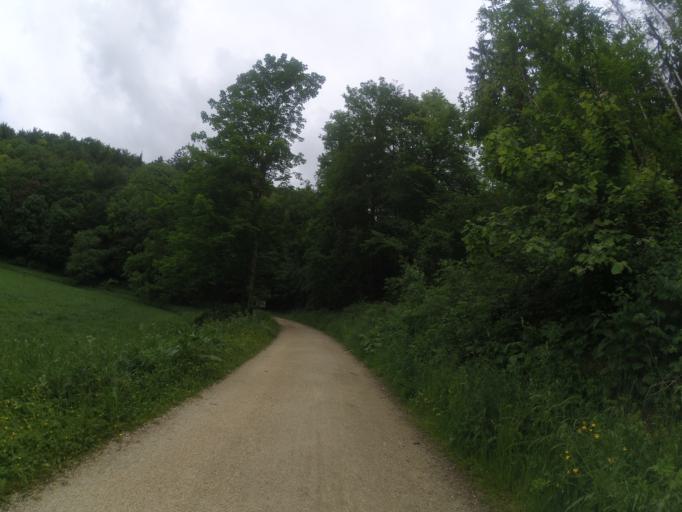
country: DE
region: Baden-Wuerttemberg
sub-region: Tuebingen Region
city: Borslingen
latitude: 48.5174
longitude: 10.0515
